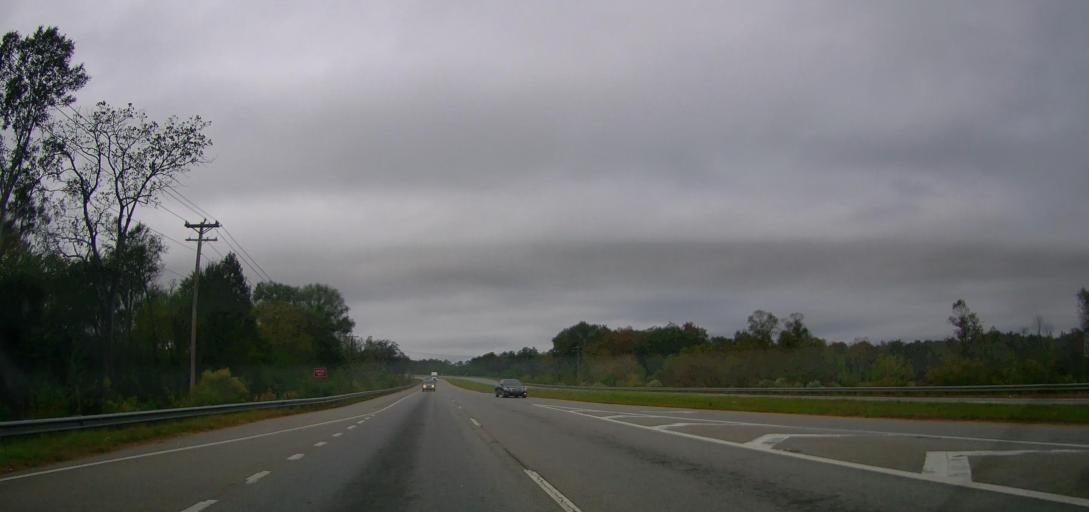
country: US
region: Georgia
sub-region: Thomas County
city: Thomasville
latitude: 30.8749
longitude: -83.9775
